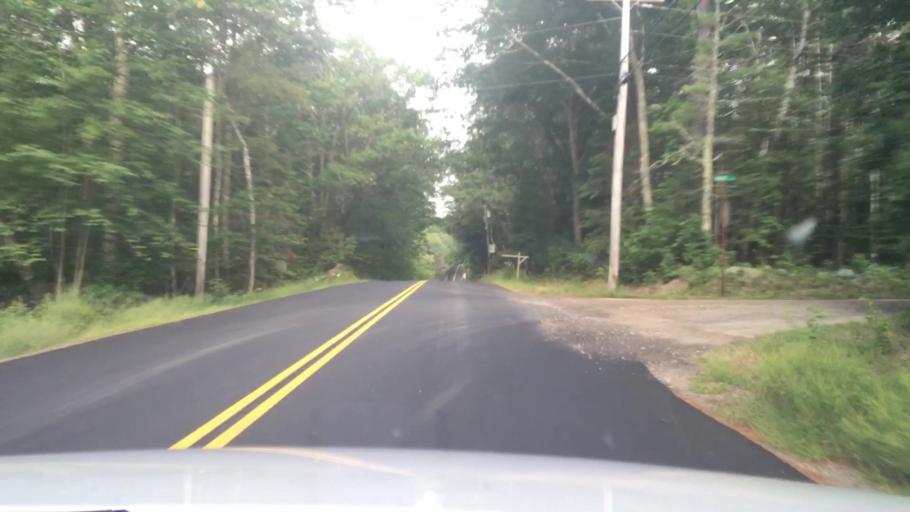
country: US
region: Maine
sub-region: Androscoggin County
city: Lisbon Falls
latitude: 44.0429
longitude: -70.0440
